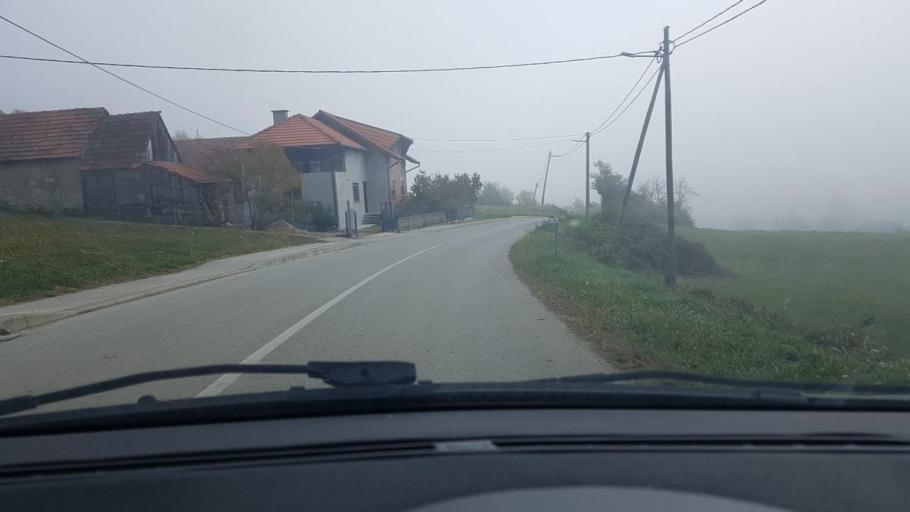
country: HR
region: Varazdinska
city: Lepoglava
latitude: 46.1526
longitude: 16.0432
